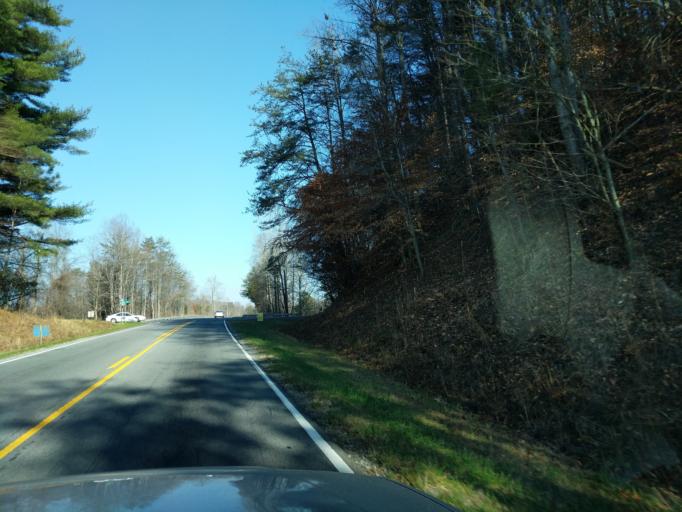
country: US
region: North Carolina
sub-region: McDowell County
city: West Marion
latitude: 35.5837
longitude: -81.9814
